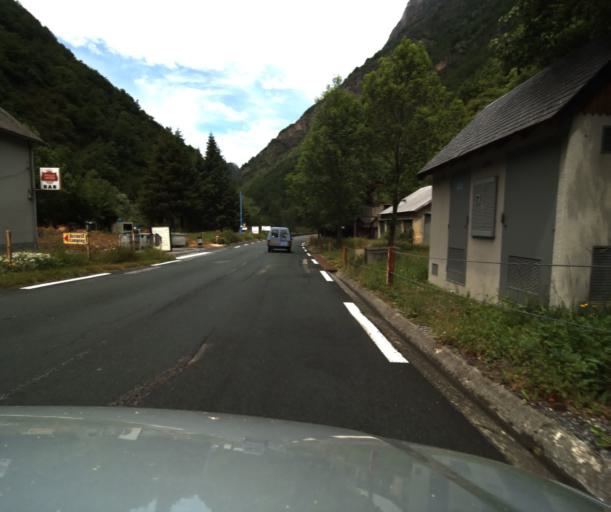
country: FR
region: Midi-Pyrenees
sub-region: Departement des Hautes-Pyrenees
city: Luz-Saint-Sauveur
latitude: 42.8013
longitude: 0.0135
